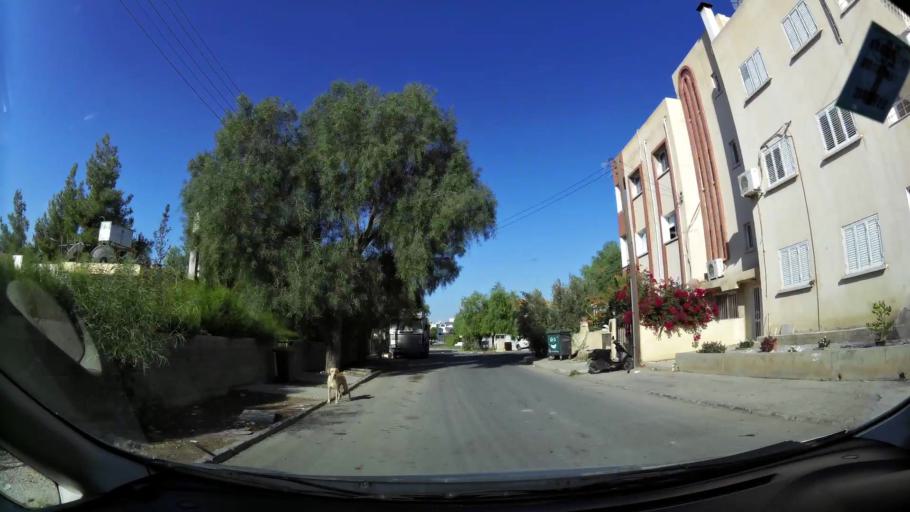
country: CY
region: Lefkosia
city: Nicosia
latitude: 35.2118
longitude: 33.3024
